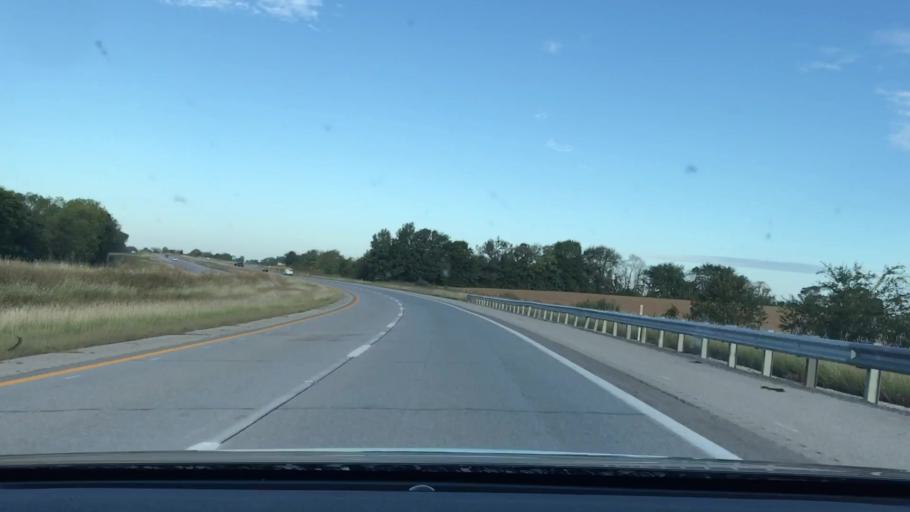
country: US
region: Kentucky
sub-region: Christian County
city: Hopkinsville
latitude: 36.8137
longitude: -87.6255
